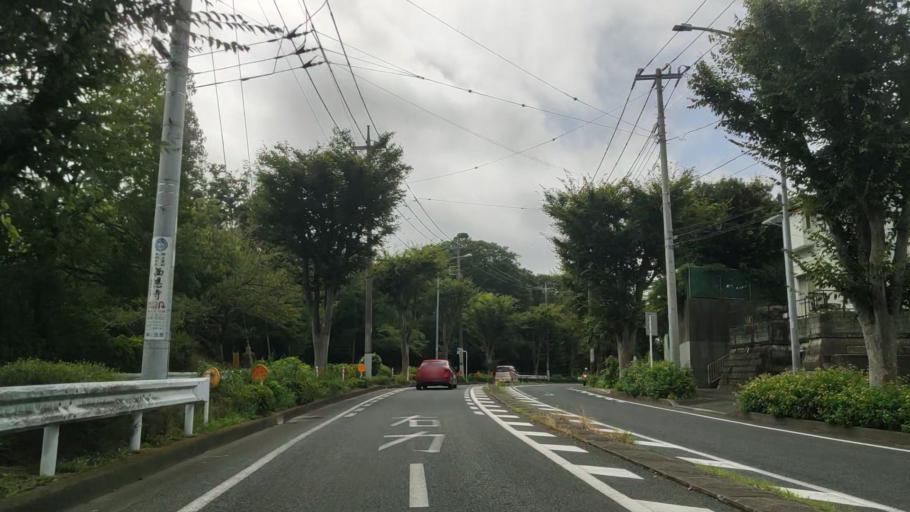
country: JP
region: Kanagawa
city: Fujisawa
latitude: 35.4097
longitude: 139.5211
